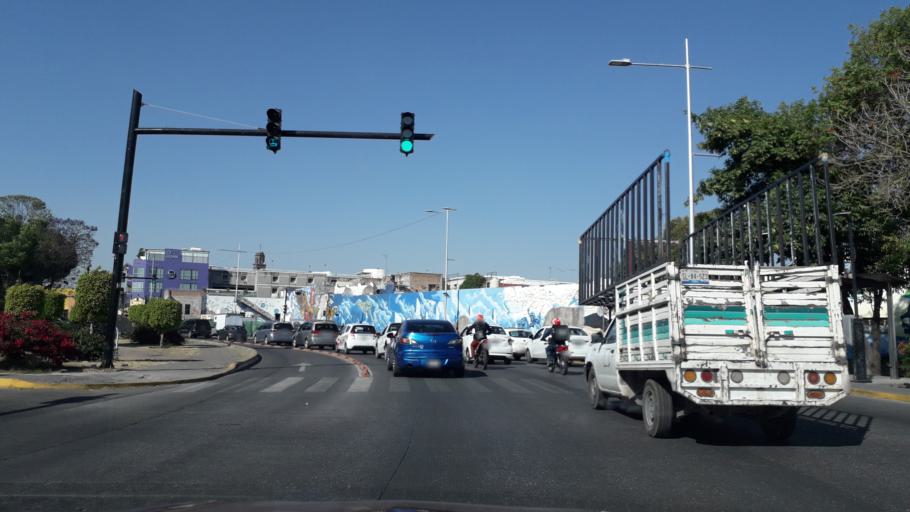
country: MX
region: Puebla
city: Puebla
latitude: 19.0408
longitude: -98.1931
